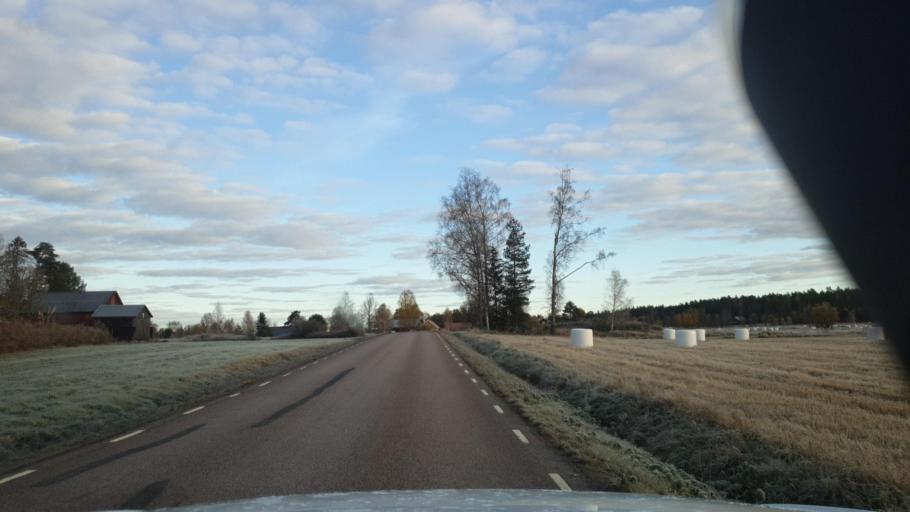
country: SE
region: Vaermland
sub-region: Eda Kommun
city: Charlottenberg
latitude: 59.7731
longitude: 12.2099
